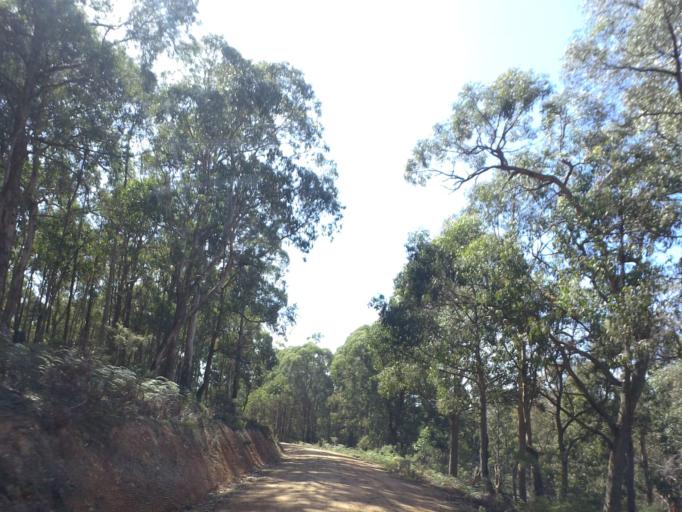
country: AU
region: Victoria
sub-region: Moorabool
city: Bacchus Marsh
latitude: -37.4384
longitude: 144.3643
